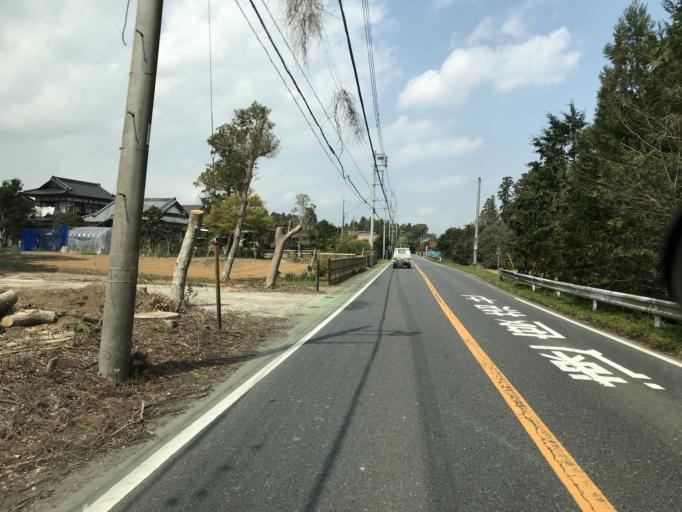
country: JP
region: Chiba
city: Sawara
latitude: 35.8687
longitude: 140.5400
